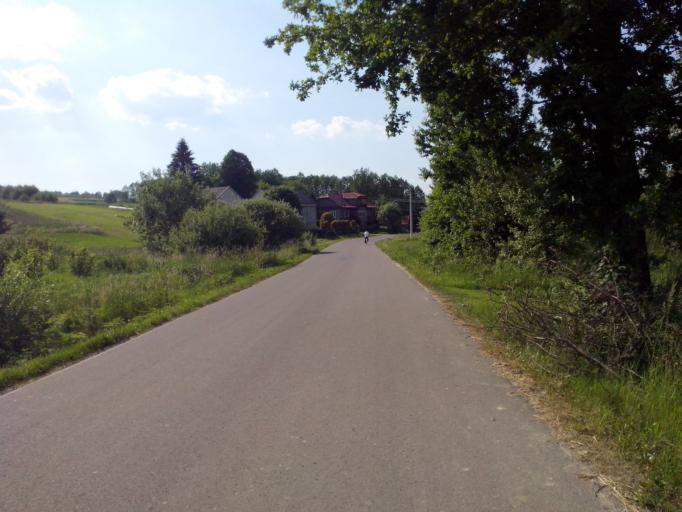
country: PL
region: Subcarpathian Voivodeship
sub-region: Powiat brzozowski
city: Blizne
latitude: 49.7474
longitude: 21.9719
